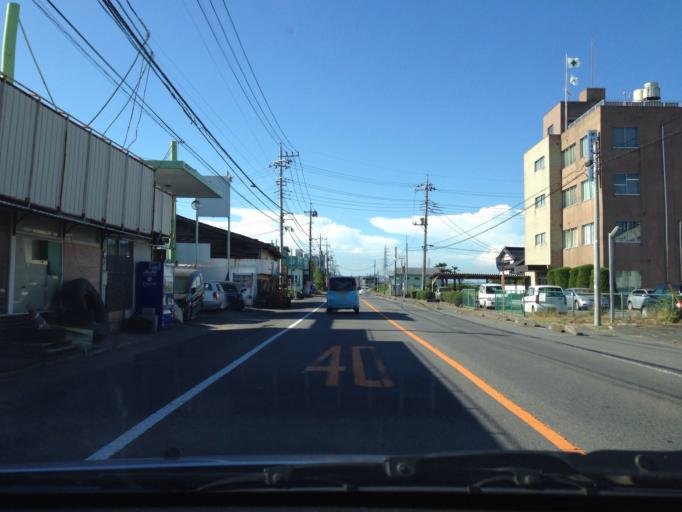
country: JP
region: Ibaraki
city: Ami
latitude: 36.0518
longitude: 140.2157
